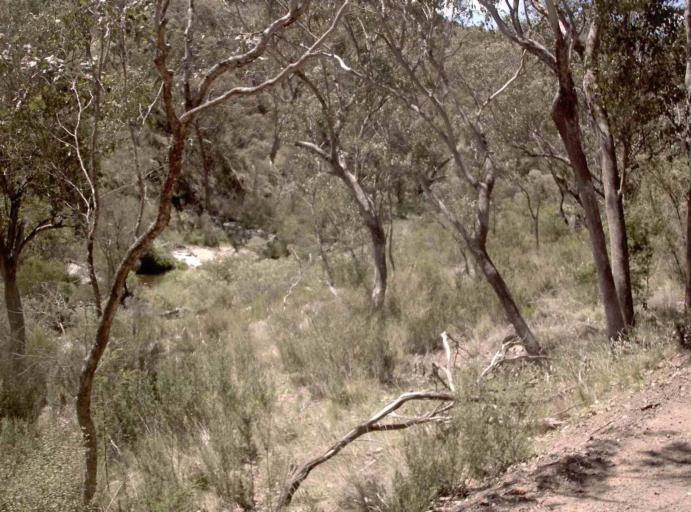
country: AU
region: New South Wales
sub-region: Snowy River
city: Jindabyne
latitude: -37.0780
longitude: 148.4907
